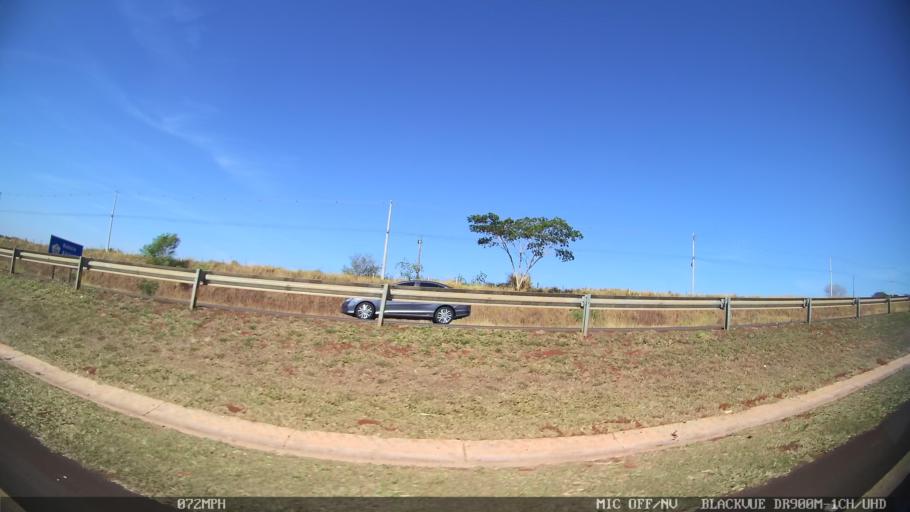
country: BR
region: Sao Paulo
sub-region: Ribeirao Preto
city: Ribeirao Preto
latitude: -21.1442
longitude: -47.8741
